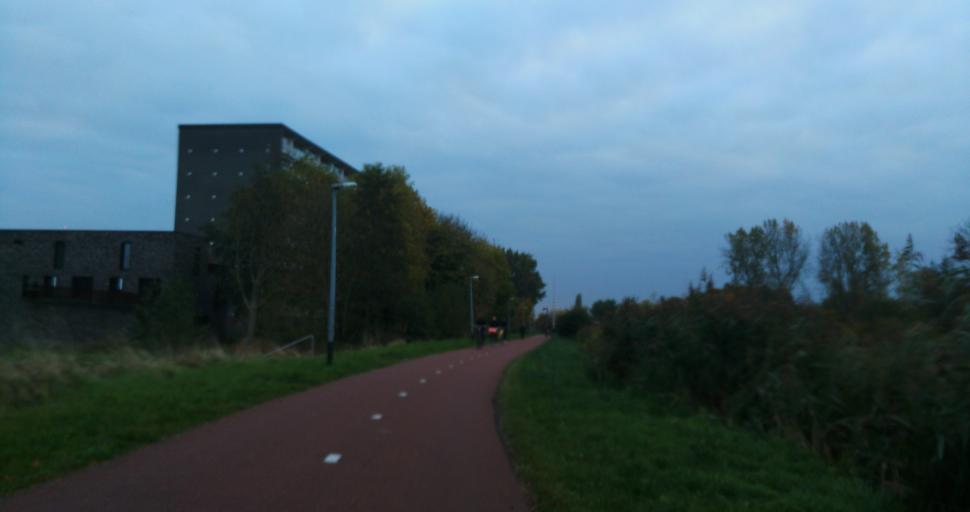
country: NL
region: Groningen
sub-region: Gemeente Groningen
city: Groningen
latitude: 53.2291
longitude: 6.5345
